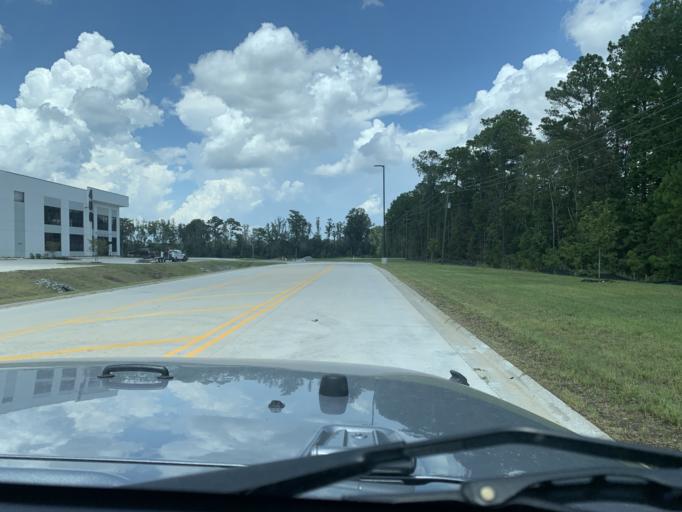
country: US
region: Georgia
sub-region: Chatham County
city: Bloomingdale
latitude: 32.1150
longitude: -81.2763
